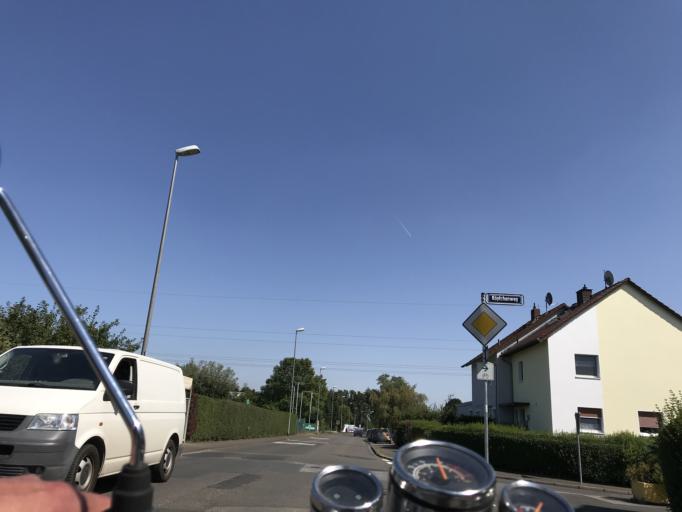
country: DE
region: Hesse
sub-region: Regierungsbezirk Darmstadt
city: Wiesbaden
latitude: 50.0822
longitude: 8.2905
